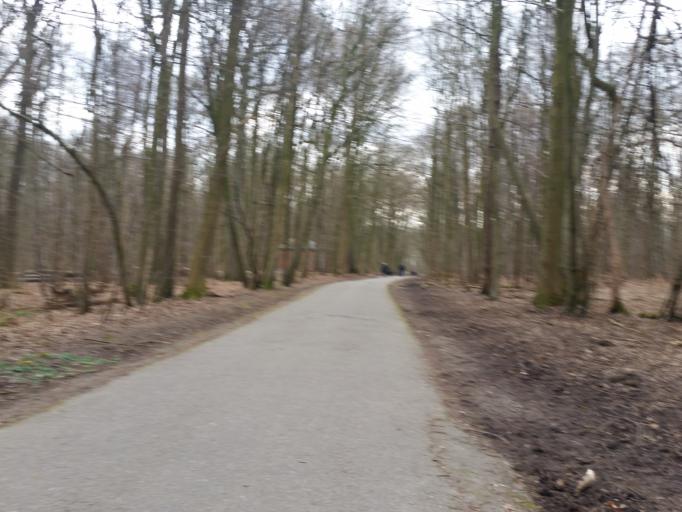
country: BE
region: Flanders
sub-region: Provincie Vlaams-Brabant
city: Sint-Genesius-Rode
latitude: 50.7886
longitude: 4.3874
